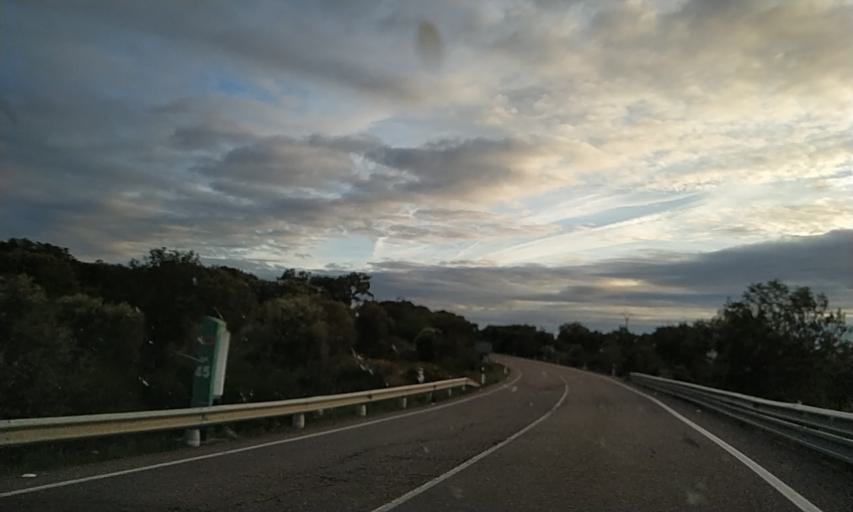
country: ES
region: Extremadura
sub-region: Provincia de Badajoz
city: La Roca de la Sierra
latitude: 39.1363
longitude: -6.6603
